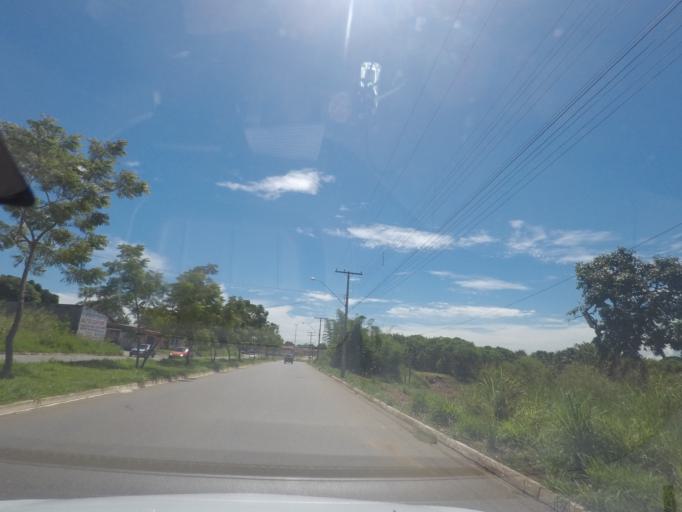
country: BR
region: Goias
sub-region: Aparecida De Goiania
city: Aparecida de Goiania
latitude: -16.7745
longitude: -49.3270
